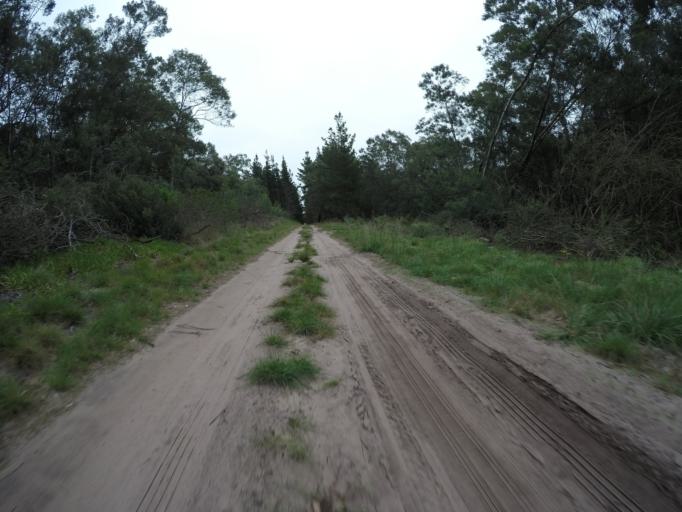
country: ZA
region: Western Cape
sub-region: Eden District Municipality
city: Knysna
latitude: -34.0090
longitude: 22.8091
